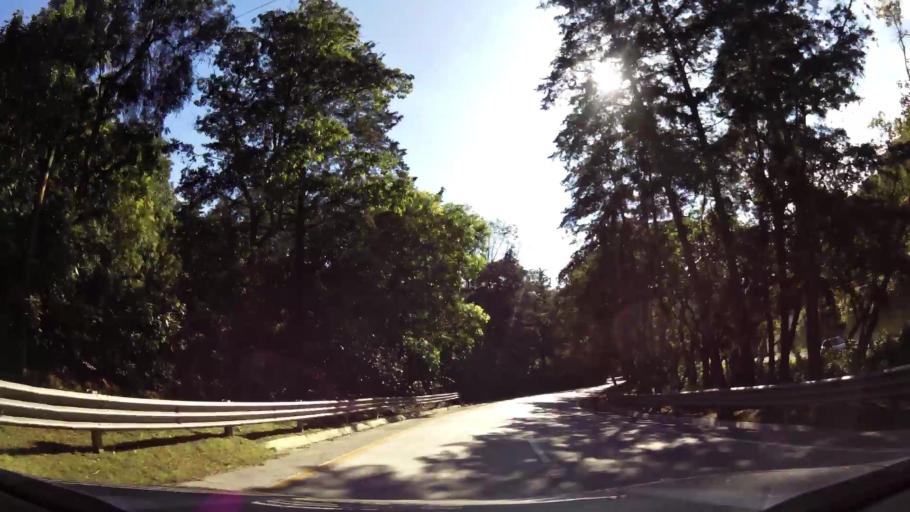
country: GT
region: Sacatepequez
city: Santa Lucia Milpas Altas
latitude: 14.5621
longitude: -90.7024
